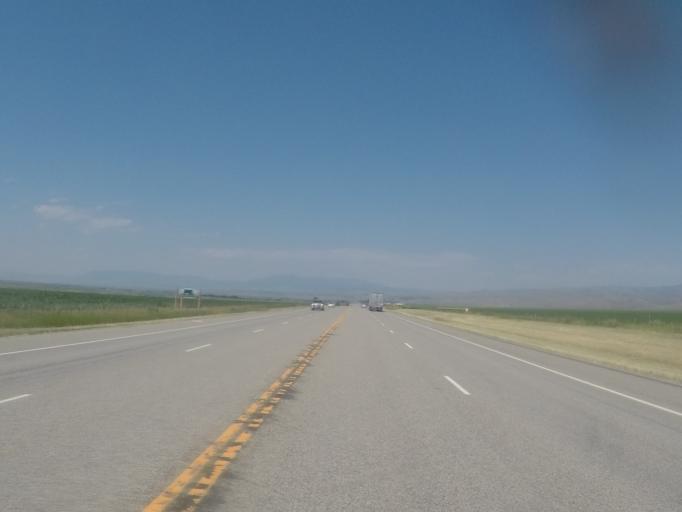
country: US
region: Montana
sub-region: Broadwater County
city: Townsend
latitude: 46.1139
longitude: -111.5042
